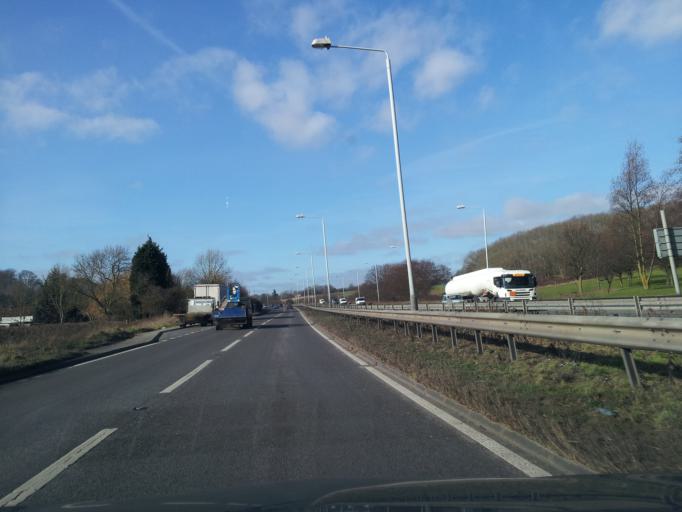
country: GB
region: England
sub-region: Nottinghamshire
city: Ruddington
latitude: 52.9030
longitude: -1.1277
